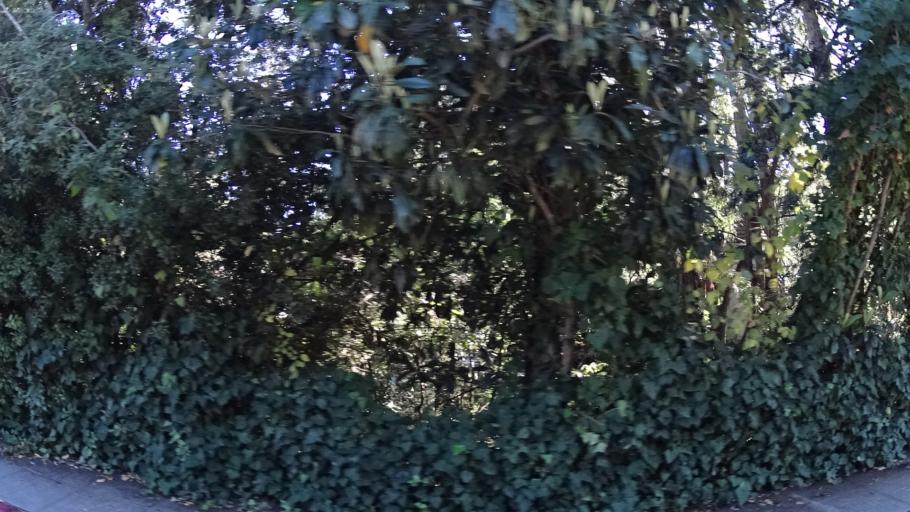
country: US
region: California
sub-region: Alameda County
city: Piedmont
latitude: 37.8198
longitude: -122.2295
